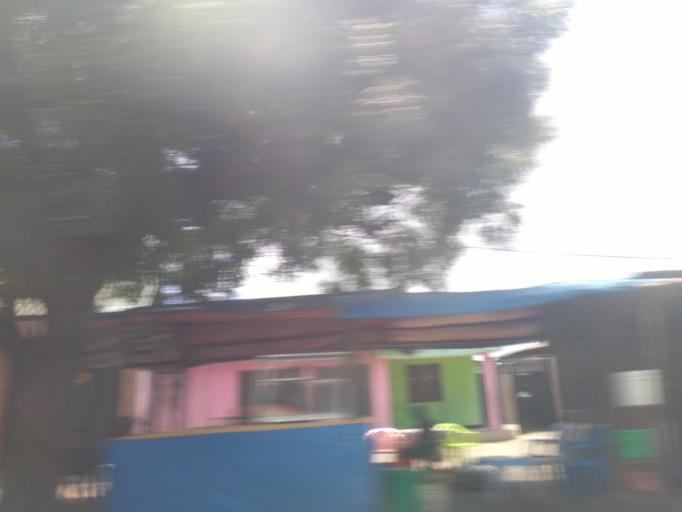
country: TZ
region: Dar es Salaam
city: Dar es Salaam
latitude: -6.8606
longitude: 39.2682
